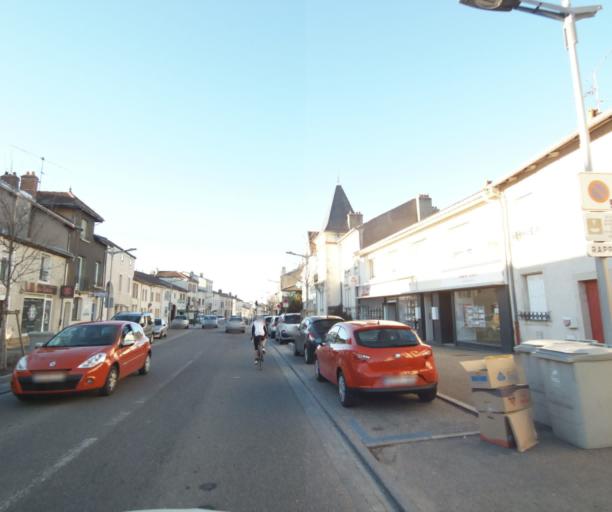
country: FR
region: Lorraine
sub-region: Departement de Meurthe-et-Moselle
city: Laneuveville-devant-Nancy
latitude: 48.6557
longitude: 6.2318
